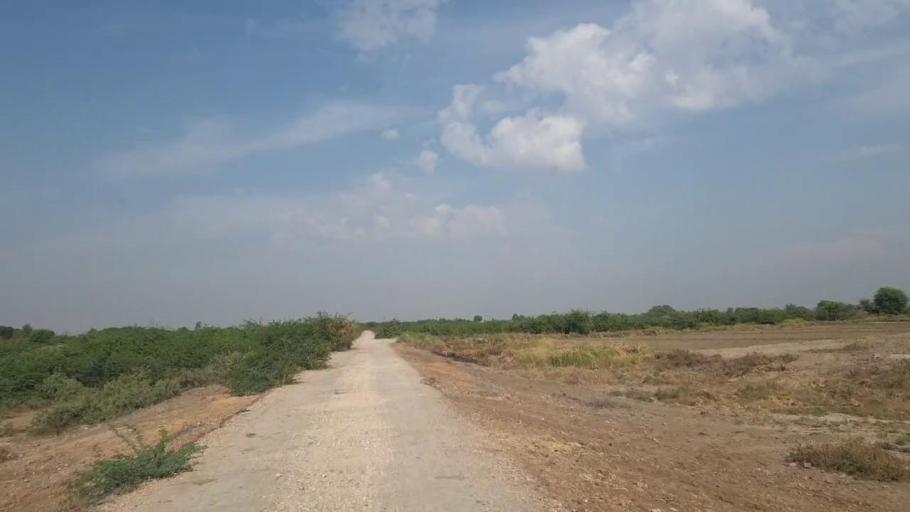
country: PK
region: Sindh
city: Digri
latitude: 24.9993
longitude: 69.0615
